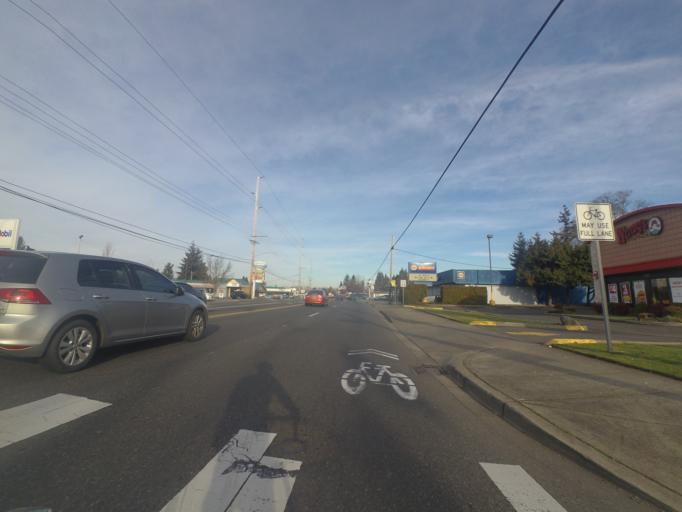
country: US
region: Washington
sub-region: Pierce County
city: Lakewood
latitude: 47.1595
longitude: -122.5045
